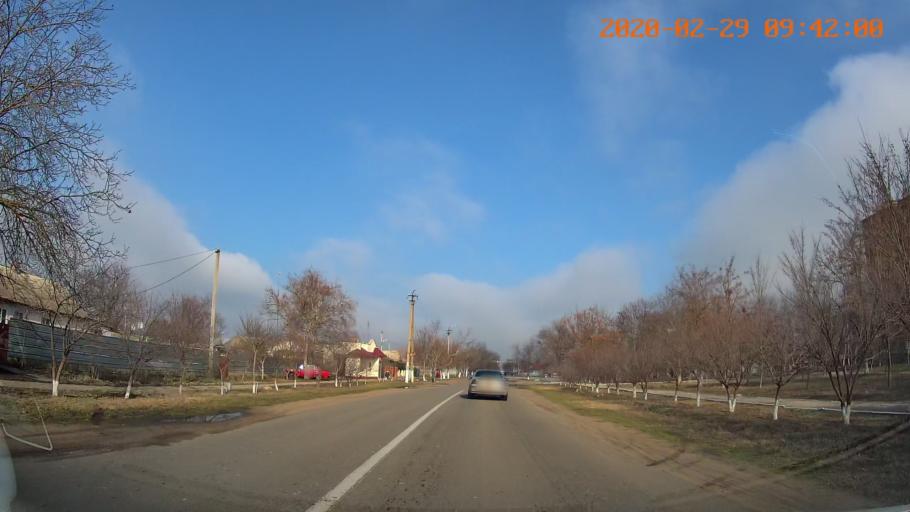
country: MD
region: Telenesti
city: Crasnoe
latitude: 46.6385
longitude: 29.8256
